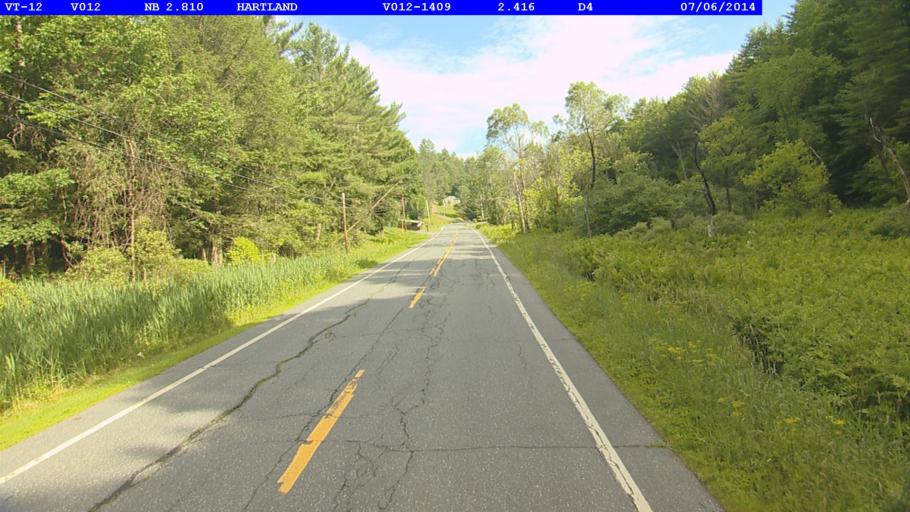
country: US
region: Vermont
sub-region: Windsor County
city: Windsor
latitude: 43.5543
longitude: -72.4394
